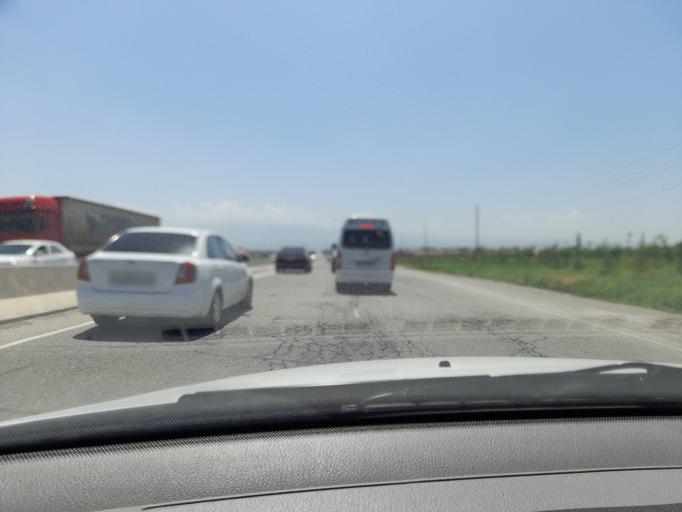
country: UZ
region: Jizzax
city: Jizzax
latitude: 40.1589
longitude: 67.9586
